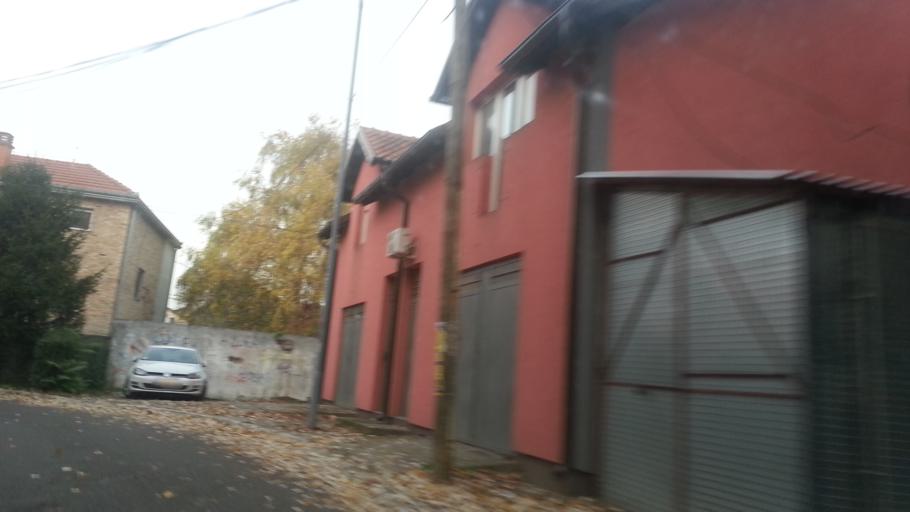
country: RS
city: Novi Banovci
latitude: 44.8945
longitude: 20.2954
